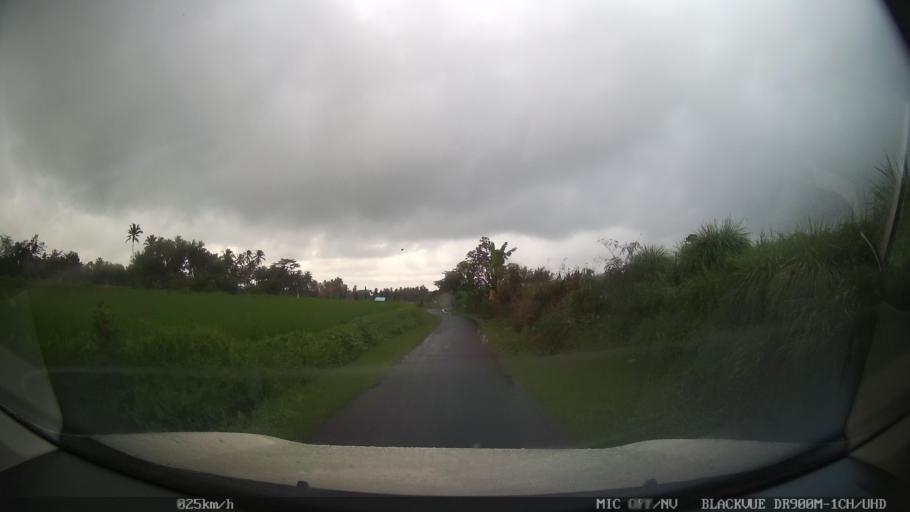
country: ID
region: Bali
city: Kekeran
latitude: -8.4813
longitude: 115.1881
